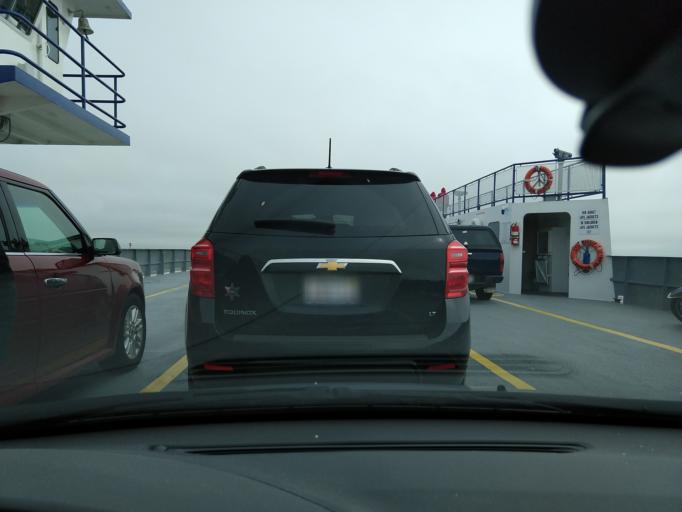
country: US
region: Alabama
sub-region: Mobile County
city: Dauphin Island
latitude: 30.2511
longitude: -88.0684
